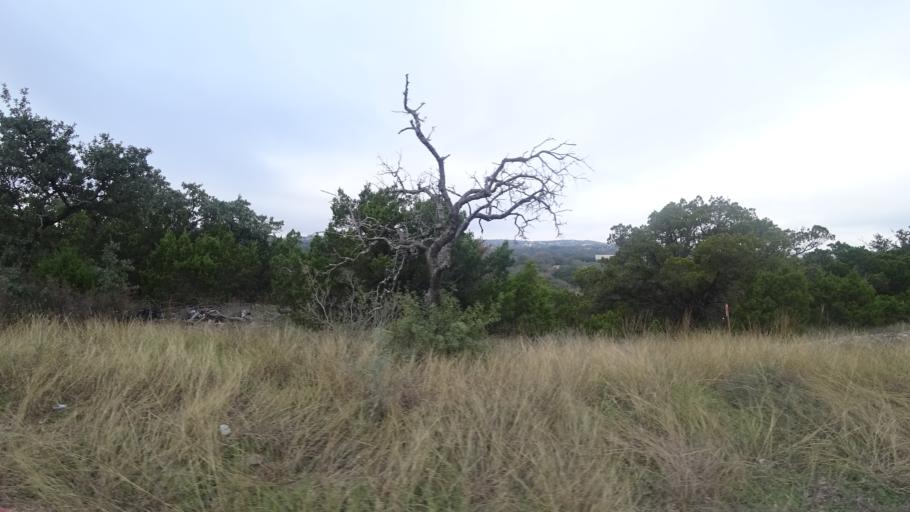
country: US
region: Texas
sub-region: Travis County
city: Bee Cave
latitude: 30.3037
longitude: -97.9345
